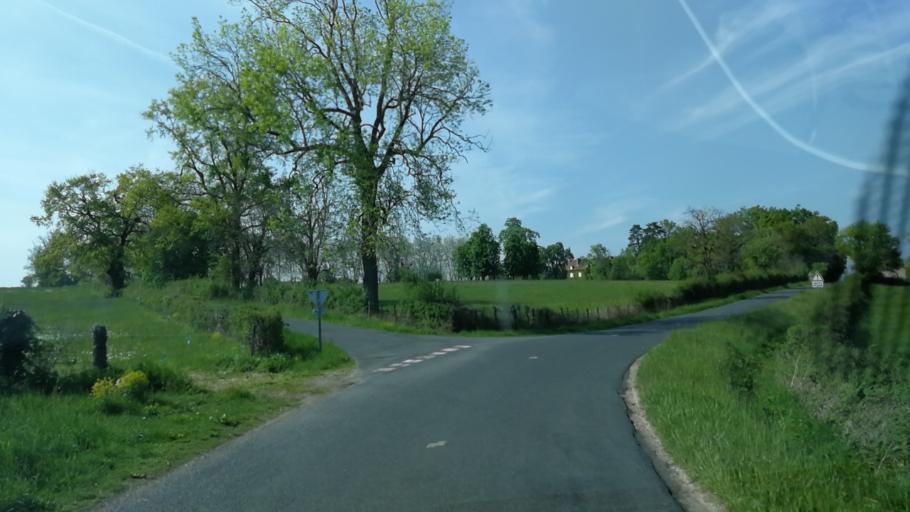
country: FR
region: Auvergne
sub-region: Departement de l'Allier
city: Saint-Gerand-le-Puy
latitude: 46.3883
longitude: 3.5806
